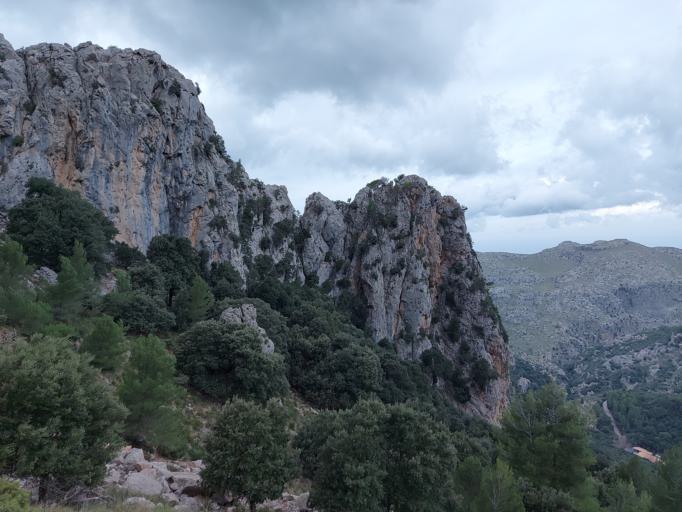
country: ES
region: Balearic Islands
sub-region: Illes Balears
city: Escorca
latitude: 39.8103
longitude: 2.8341
